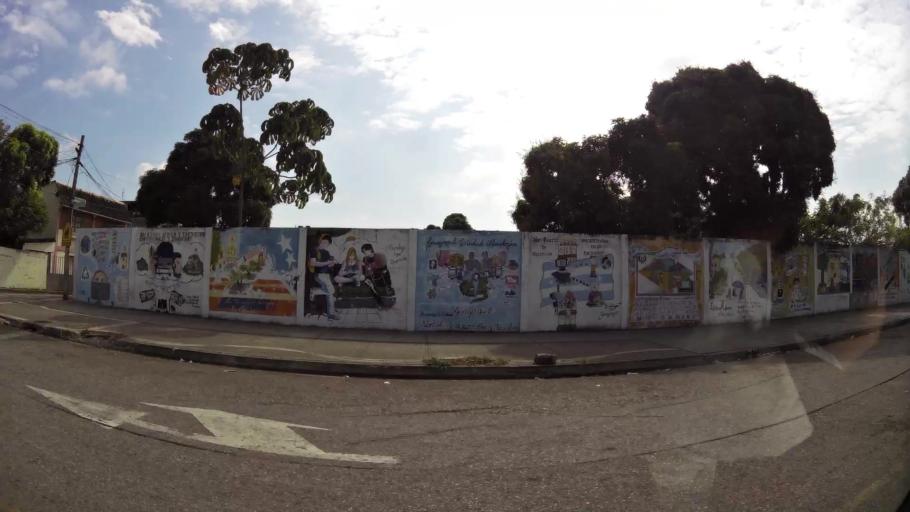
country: EC
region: Guayas
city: Guayaquil
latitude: -2.2606
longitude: -79.8917
